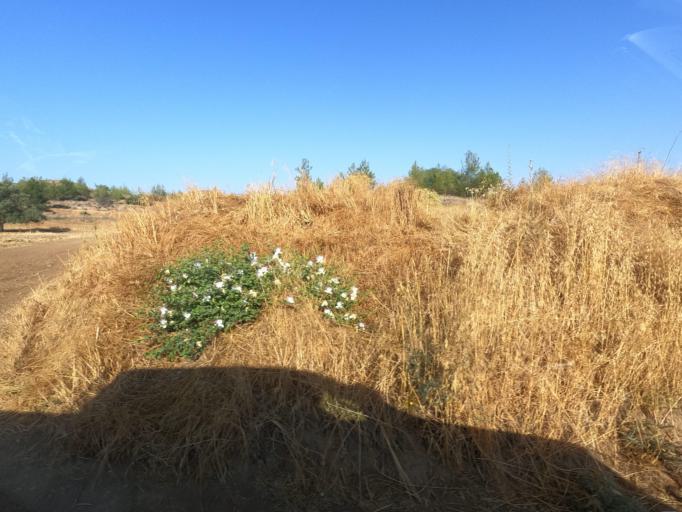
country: CY
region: Lefkosia
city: Lympia
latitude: 34.9906
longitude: 33.4373
